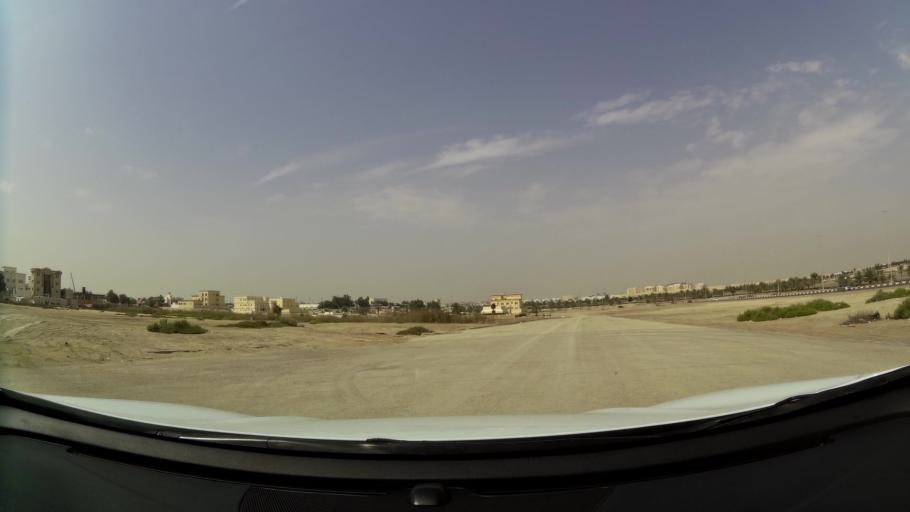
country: AE
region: Abu Dhabi
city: Abu Dhabi
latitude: 24.3021
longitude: 54.6317
